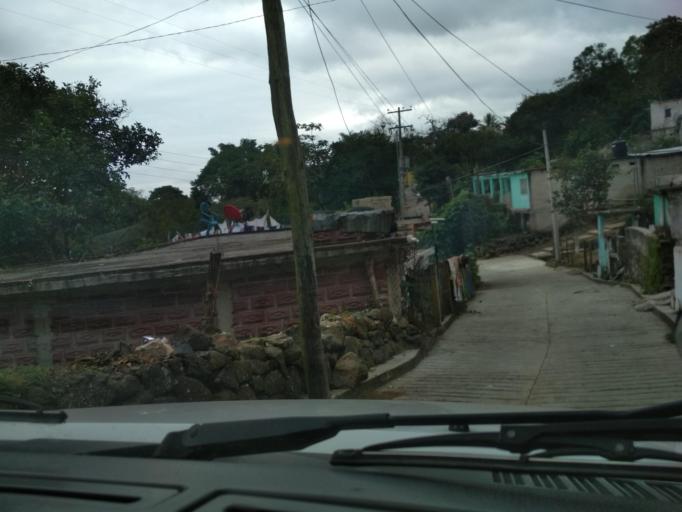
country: MX
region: Veracruz
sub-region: Naolinco
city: El Espinal
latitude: 19.5881
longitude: -96.8759
